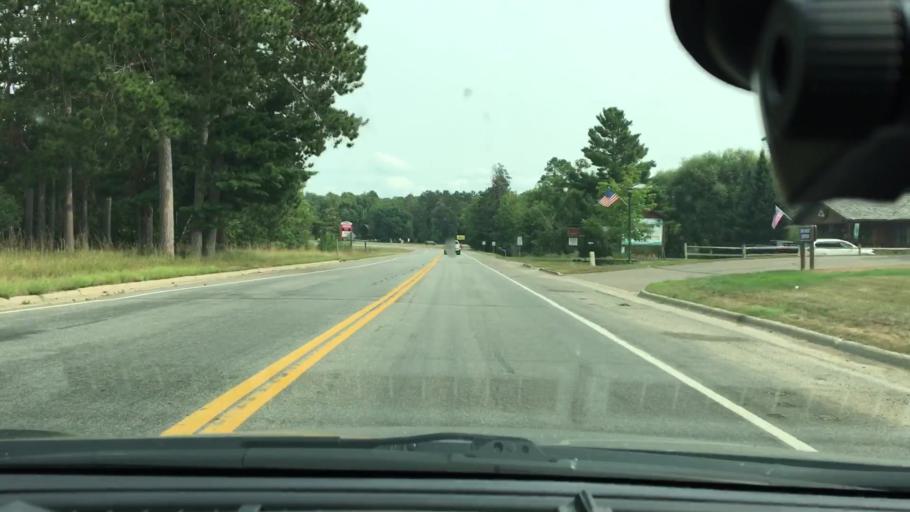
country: US
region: Minnesota
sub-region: Crow Wing County
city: Cross Lake
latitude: 46.6689
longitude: -94.1084
